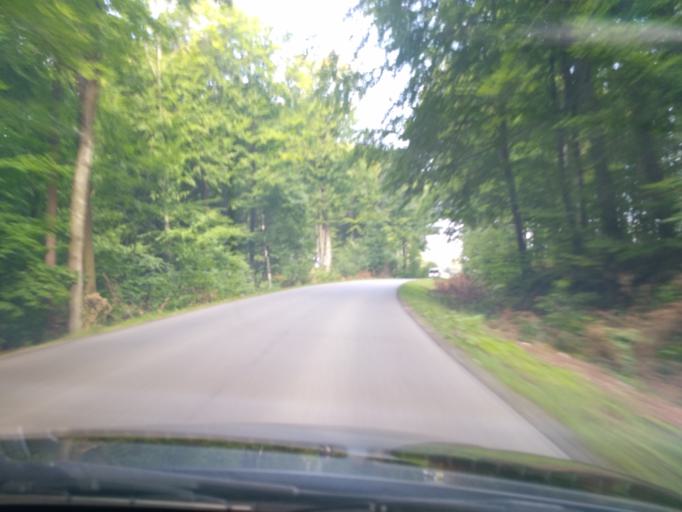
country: PL
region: Subcarpathian Voivodeship
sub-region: Powiat strzyzowski
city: Czudec
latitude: 49.9692
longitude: 21.8378
